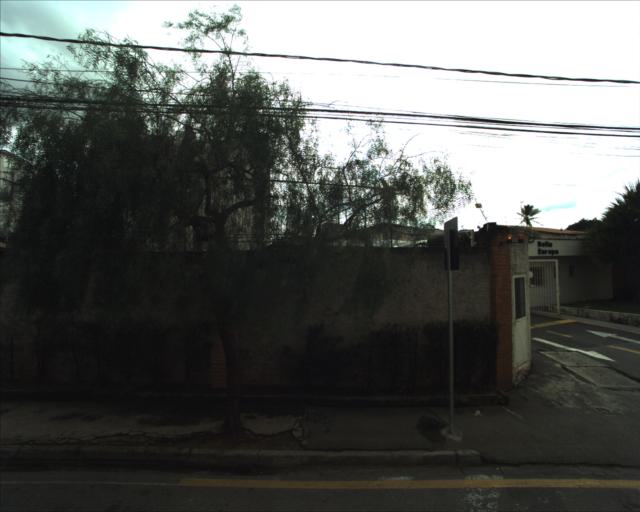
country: BR
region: Sao Paulo
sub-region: Sorocaba
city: Sorocaba
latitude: -23.5222
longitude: -47.4851
